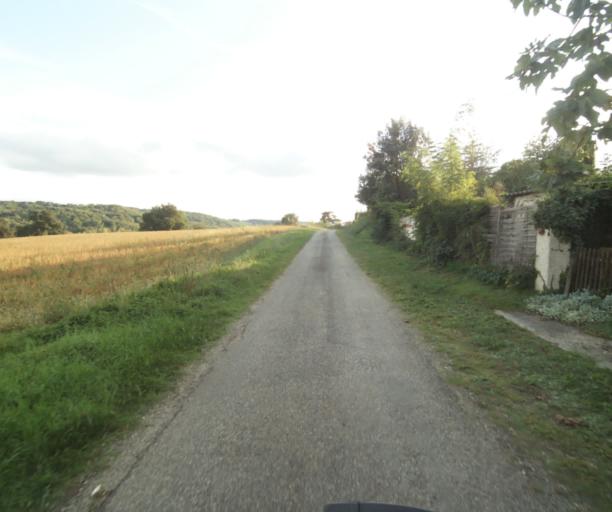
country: FR
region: Midi-Pyrenees
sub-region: Departement de la Haute-Garonne
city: Launac
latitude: 43.8214
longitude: 1.1230
